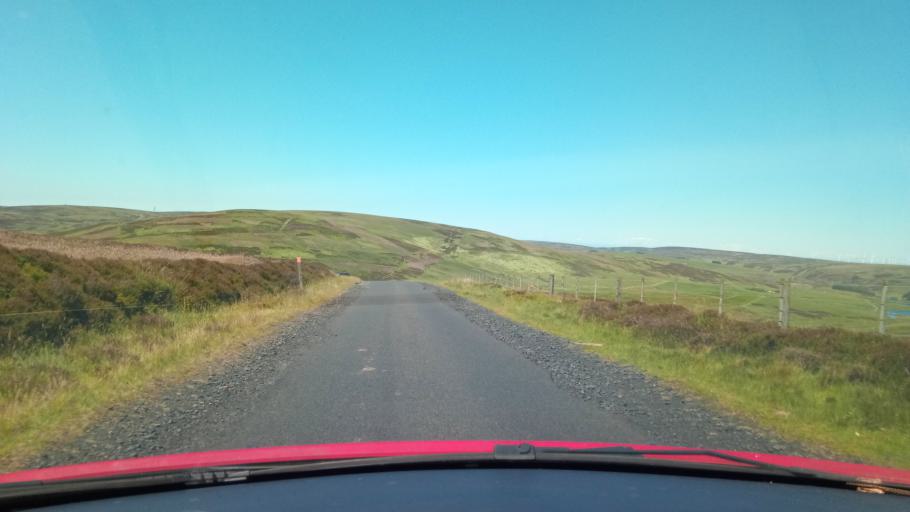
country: GB
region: Scotland
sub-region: East Lothian
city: Dunbar
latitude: 55.8445
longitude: -2.5673
